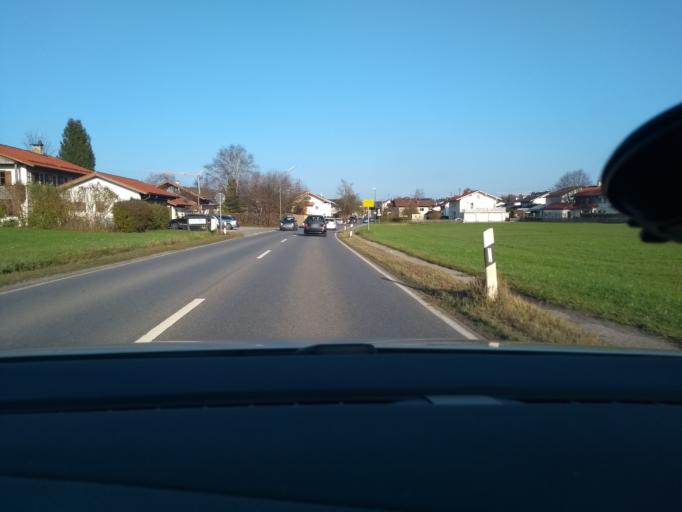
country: DE
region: Bavaria
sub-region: Upper Bavaria
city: Prutting
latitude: 47.8912
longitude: 12.1981
